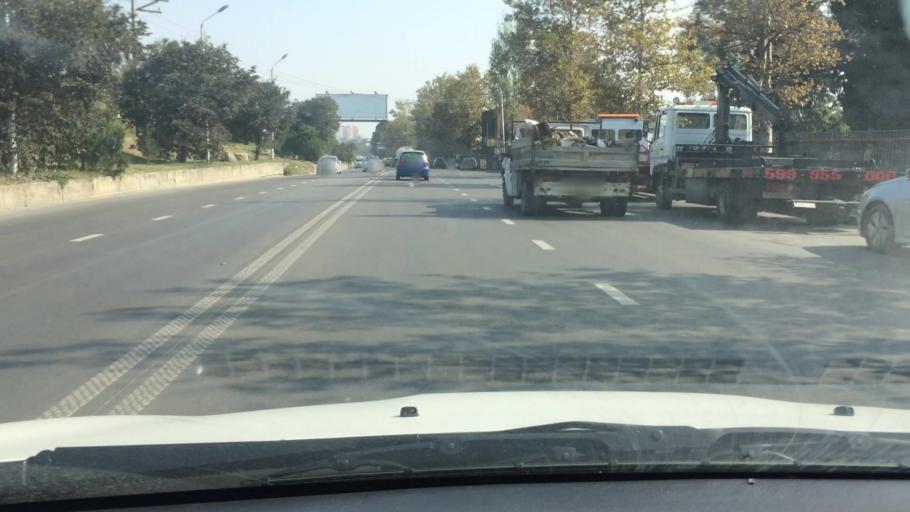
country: GE
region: T'bilisi
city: Tbilisi
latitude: 41.6920
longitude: 44.8285
